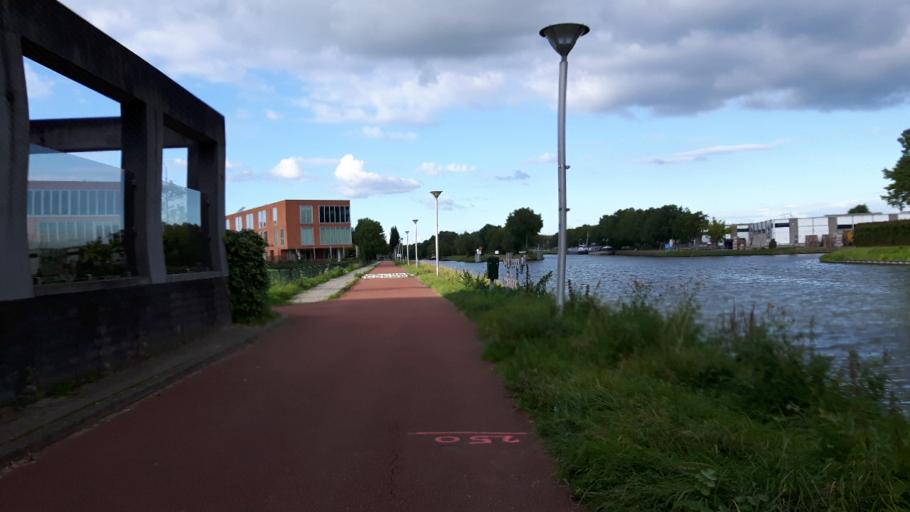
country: NL
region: Utrecht
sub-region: Gemeente Vianen
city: Vianen
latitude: 51.9865
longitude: 5.0964
